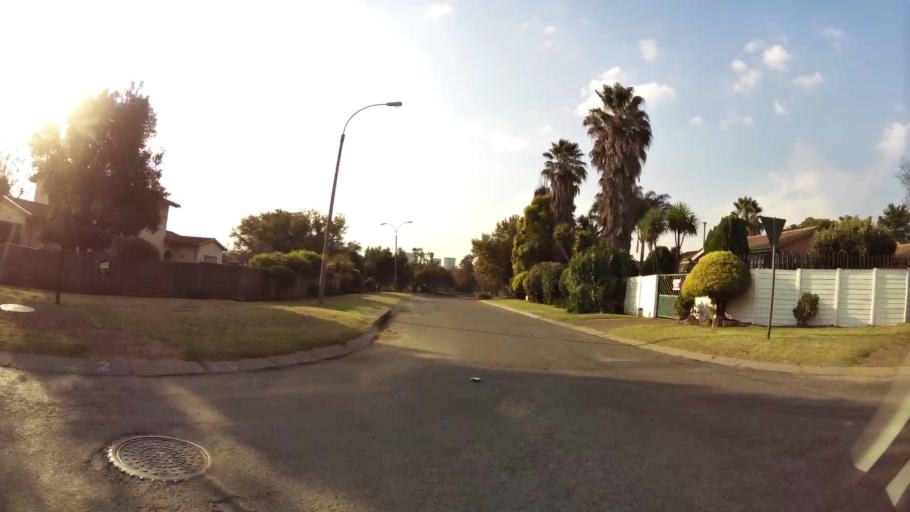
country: ZA
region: Gauteng
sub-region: City of Johannesburg Metropolitan Municipality
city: Modderfontein
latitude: -26.1310
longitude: 28.1942
